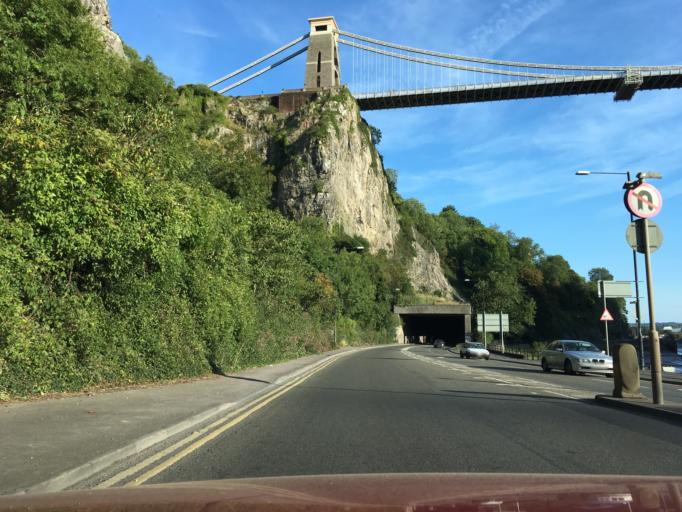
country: GB
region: England
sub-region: Bristol
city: Bristol
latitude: 51.4566
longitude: -2.6285
